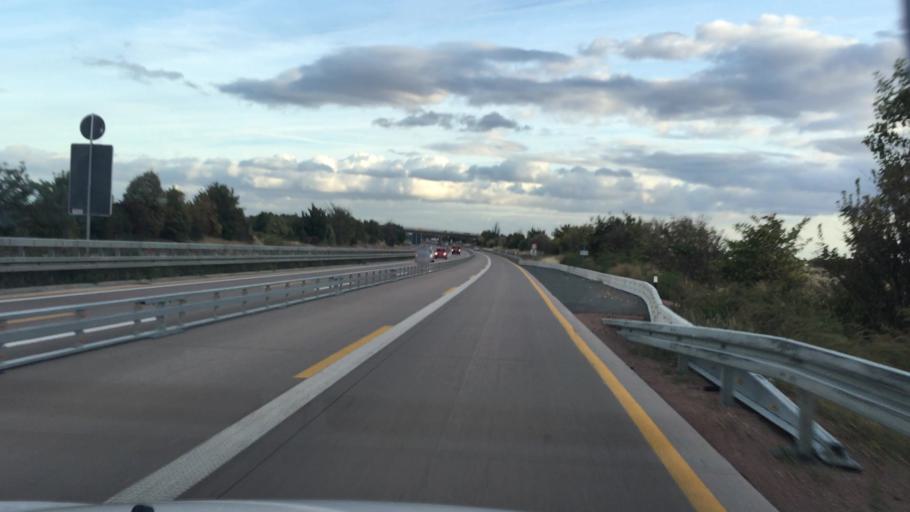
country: DE
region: Saxony-Anhalt
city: Nauendorf
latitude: 51.5932
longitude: 11.8735
